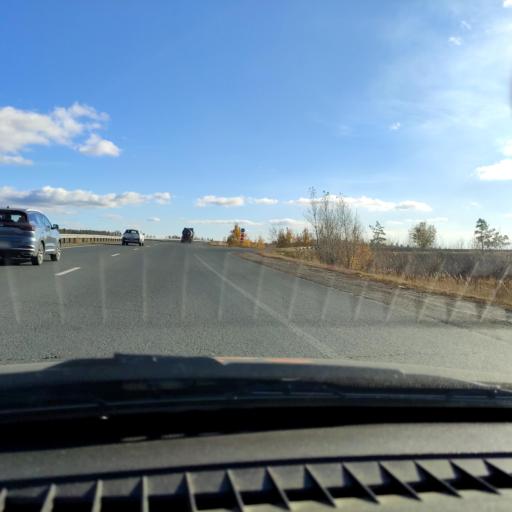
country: RU
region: Samara
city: Zhigulevsk
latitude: 53.5170
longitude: 49.5355
